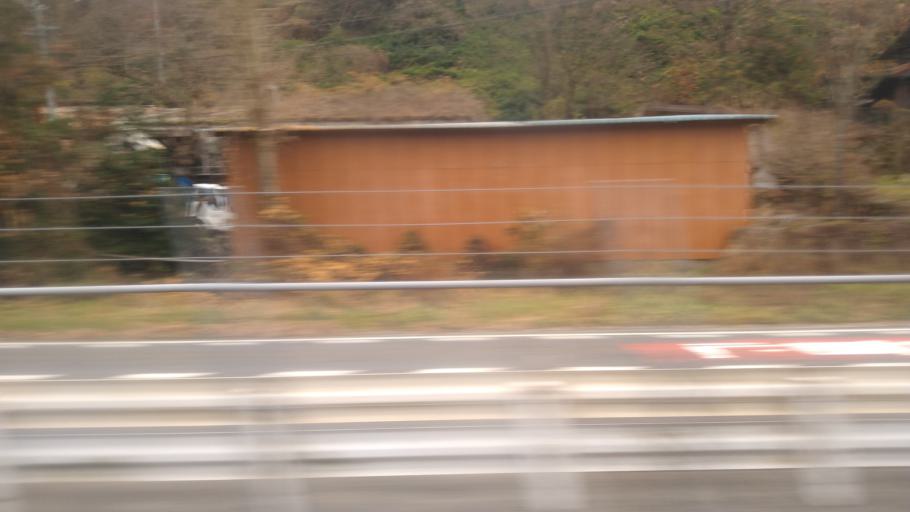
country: JP
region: Gifu
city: Nakatsugawa
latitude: 35.6491
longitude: 137.6180
